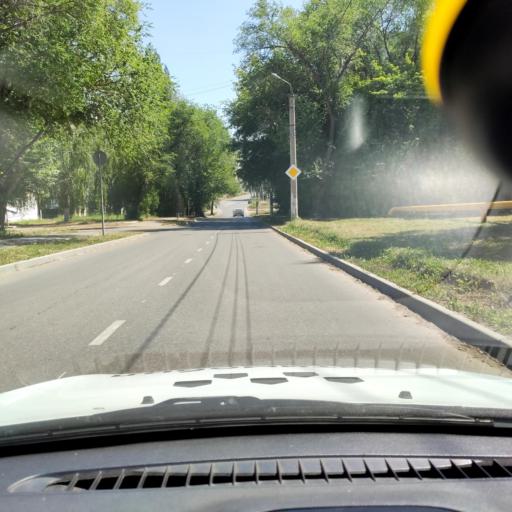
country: RU
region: Samara
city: Zhigulevsk
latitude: 53.3977
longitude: 49.5066
